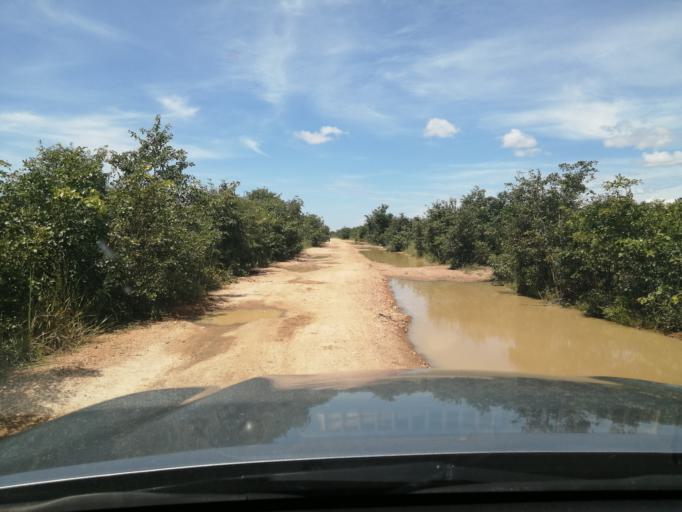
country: ZM
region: Central
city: Chibombo
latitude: -15.0395
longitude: 27.8248
